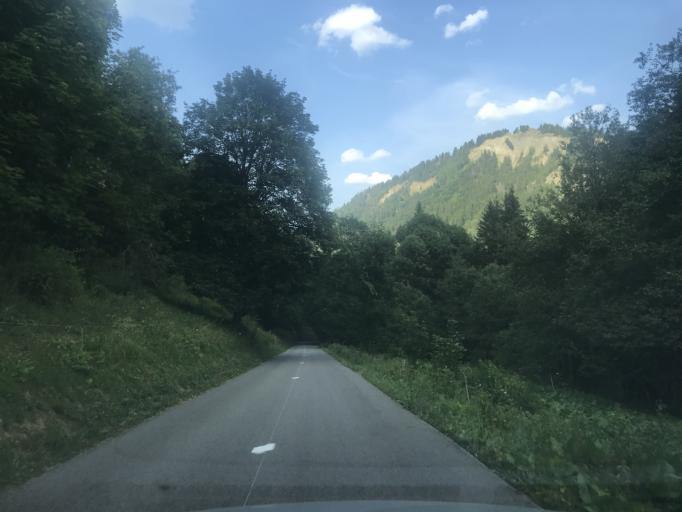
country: FR
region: Rhone-Alpes
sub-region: Departement de la Savoie
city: Saint-Etienne-de-Cuines
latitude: 45.2747
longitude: 6.2034
